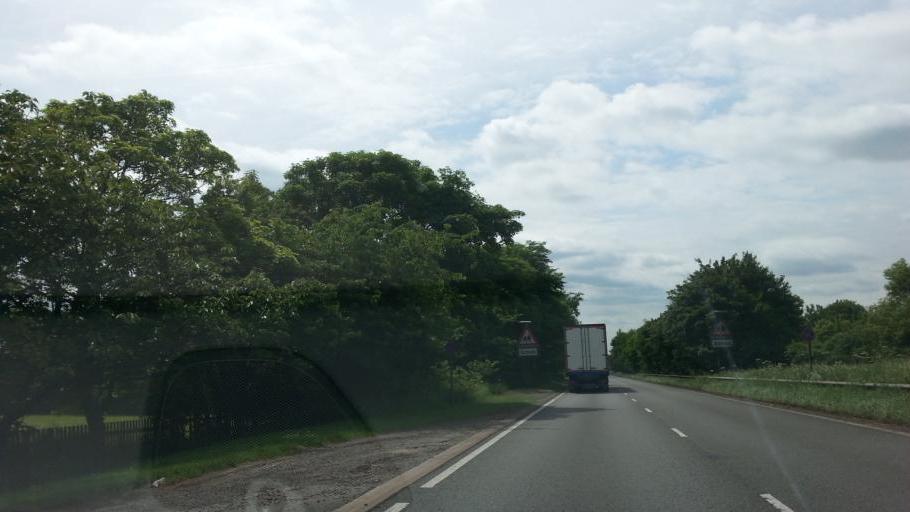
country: GB
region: England
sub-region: Leicestershire
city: Queniborough
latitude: 52.7309
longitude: -1.0705
